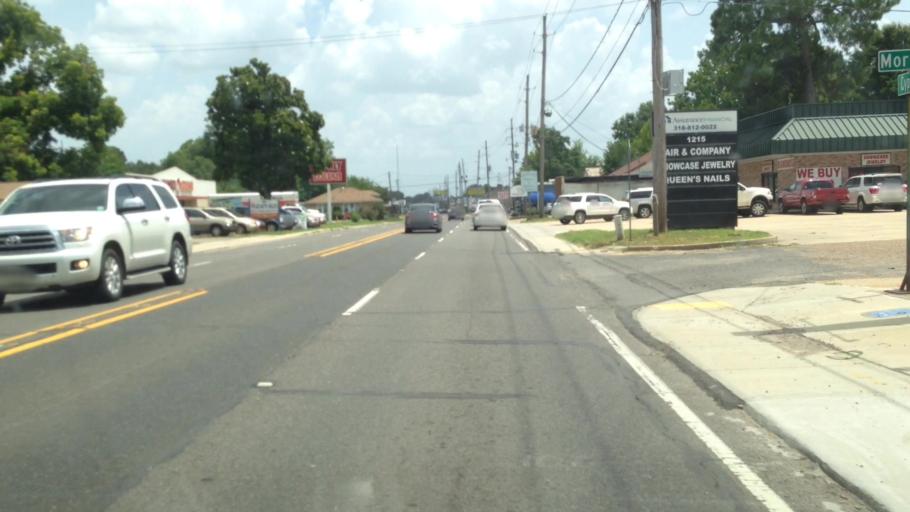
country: US
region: Louisiana
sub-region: Ouachita Parish
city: Monroe
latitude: 32.5105
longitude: -92.1340
